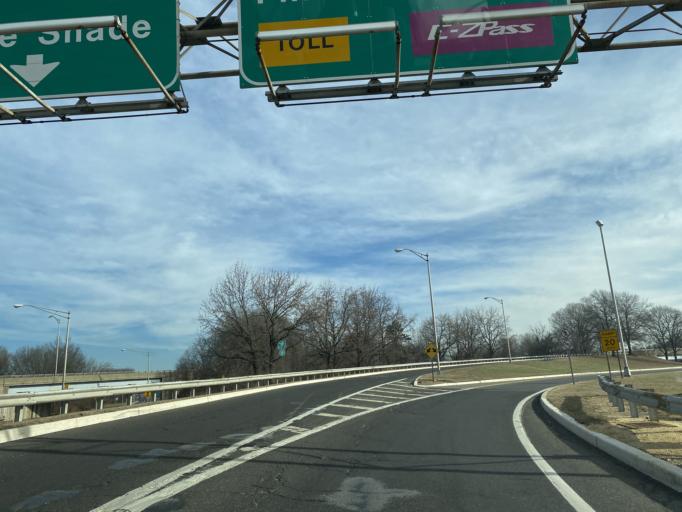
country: US
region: New Jersey
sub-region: Camden County
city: Pennsauken
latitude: 39.9740
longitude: -75.0352
